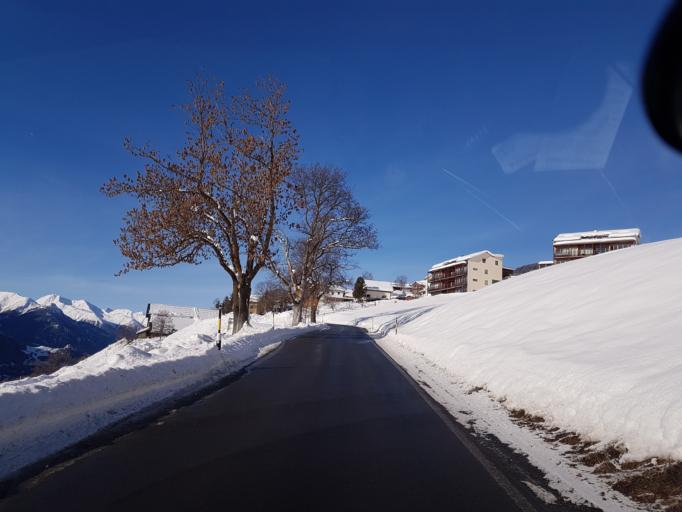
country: CH
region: Grisons
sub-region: Inn District
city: Scuol
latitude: 46.8168
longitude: 10.3440
